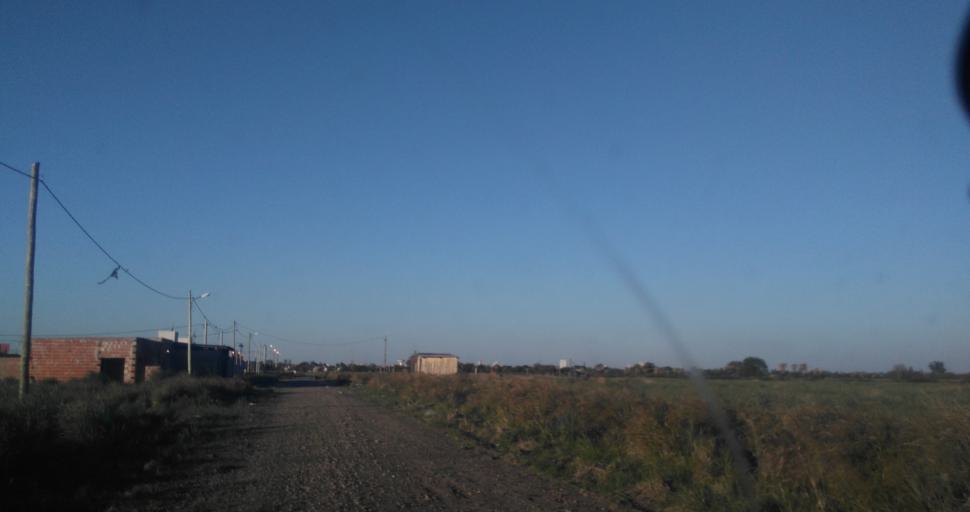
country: AR
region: Chaco
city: Resistencia
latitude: -27.4766
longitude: -59.0274
